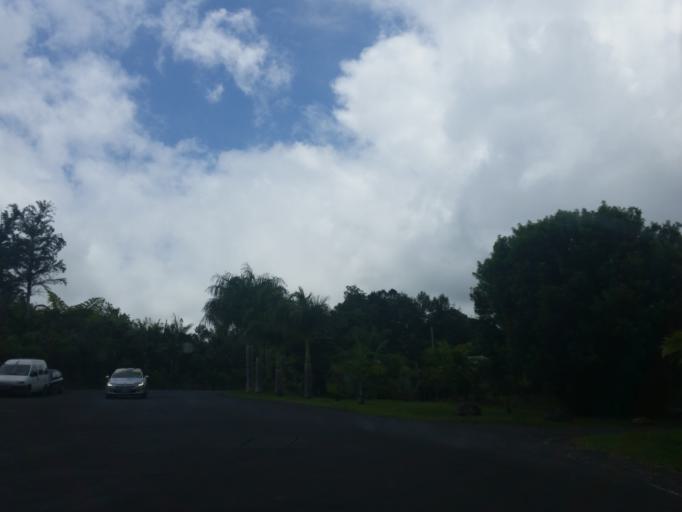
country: RE
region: Reunion
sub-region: Reunion
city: L'Entre-Deux
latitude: -21.2553
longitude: 55.4951
